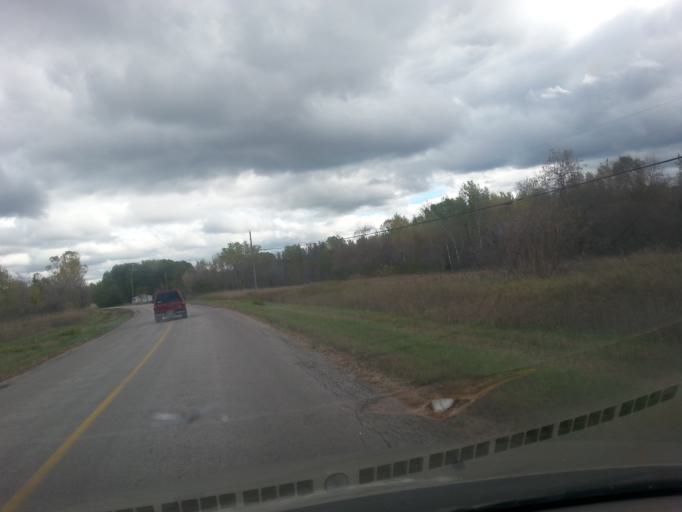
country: CA
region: Ontario
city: Pembroke
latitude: 45.5174
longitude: -77.0485
